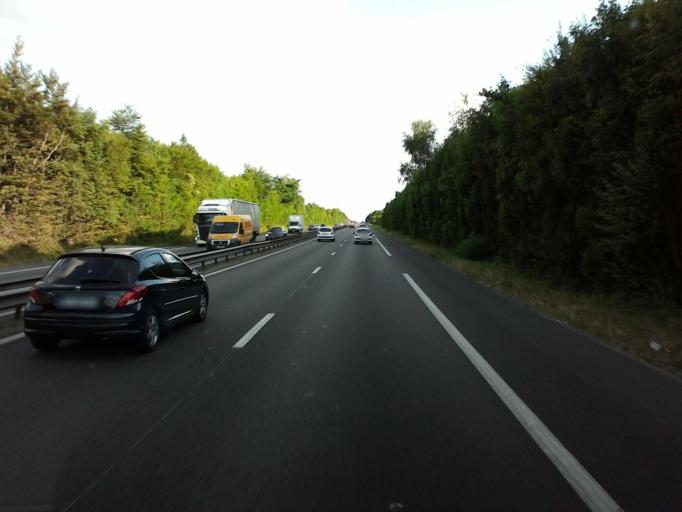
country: FR
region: Lorraine
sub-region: Departement de Meurthe-et-Moselle
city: Laxou
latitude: 48.6740
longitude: 6.1210
